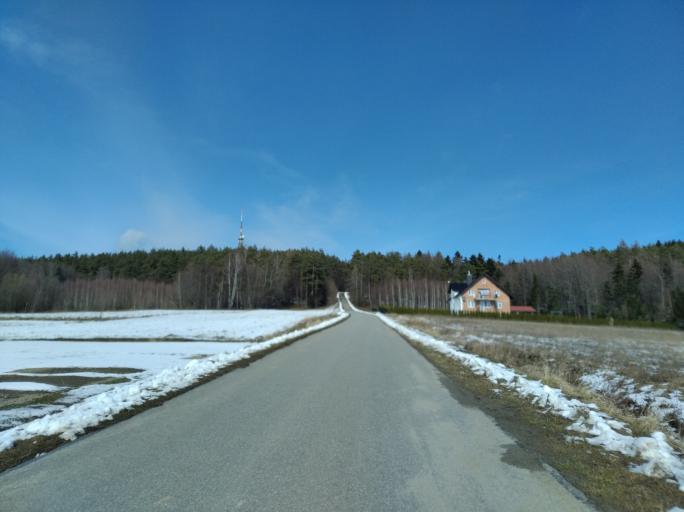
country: PL
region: Subcarpathian Voivodeship
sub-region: Powiat krosnienski
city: Korczyna
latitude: 49.7491
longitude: 21.8145
